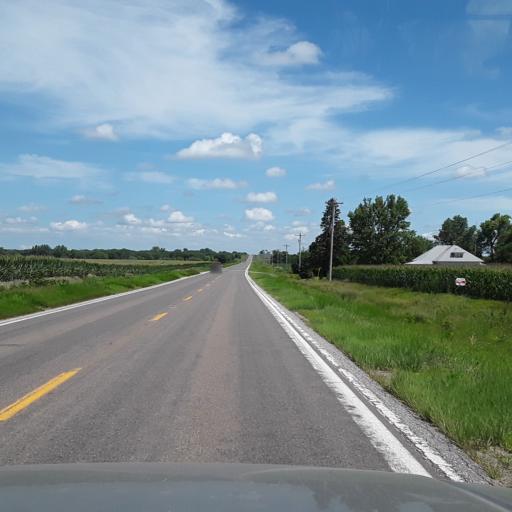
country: US
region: Nebraska
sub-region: York County
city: York
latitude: 40.9751
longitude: -97.4063
